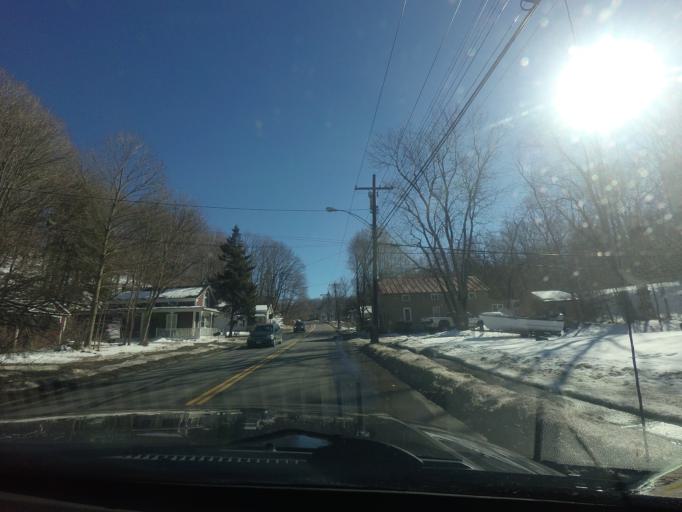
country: US
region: New York
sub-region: Rensselaer County
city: Nassau
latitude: 42.5141
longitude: -73.6059
